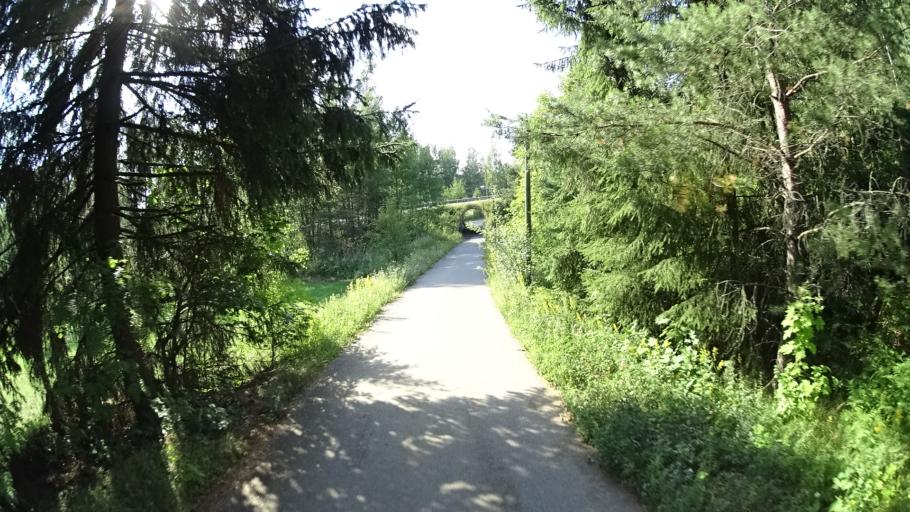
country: FI
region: Uusimaa
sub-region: Porvoo
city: Porvoo
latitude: 60.4106
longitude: 25.6479
